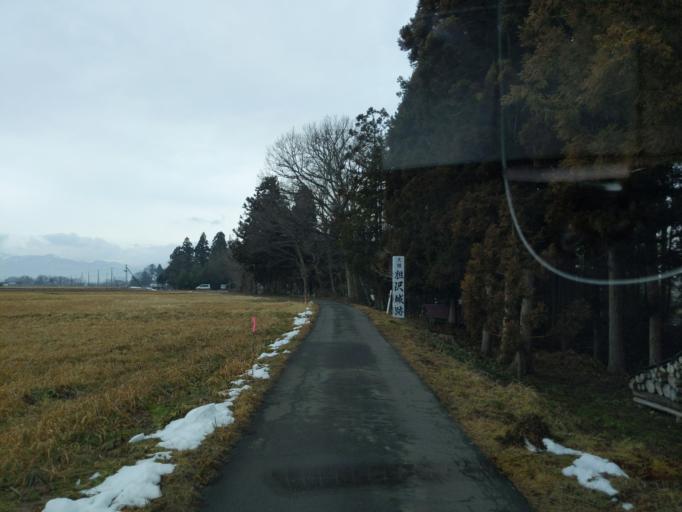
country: JP
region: Iwate
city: Mizusawa
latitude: 39.1833
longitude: 141.1393
